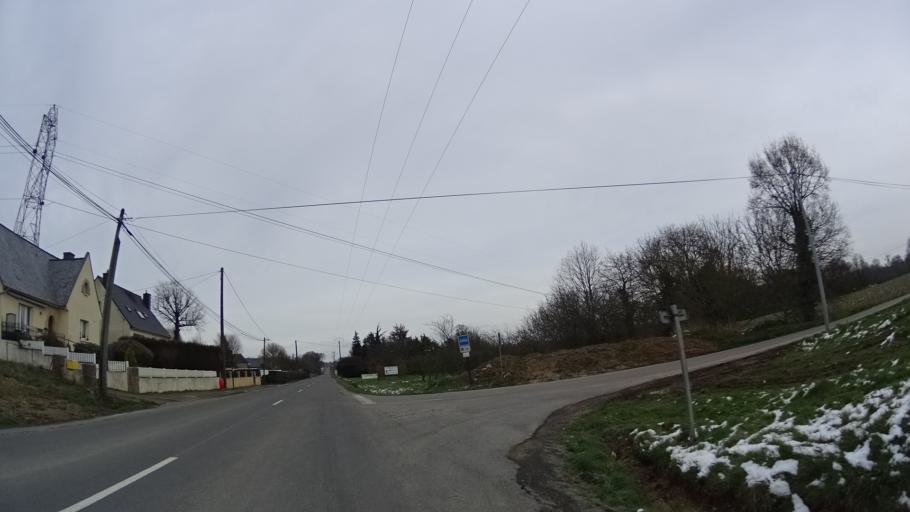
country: FR
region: Brittany
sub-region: Departement d'Ille-et-Vilaine
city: Montauban-de-Bretagne
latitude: 48.2375
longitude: -2.0120
